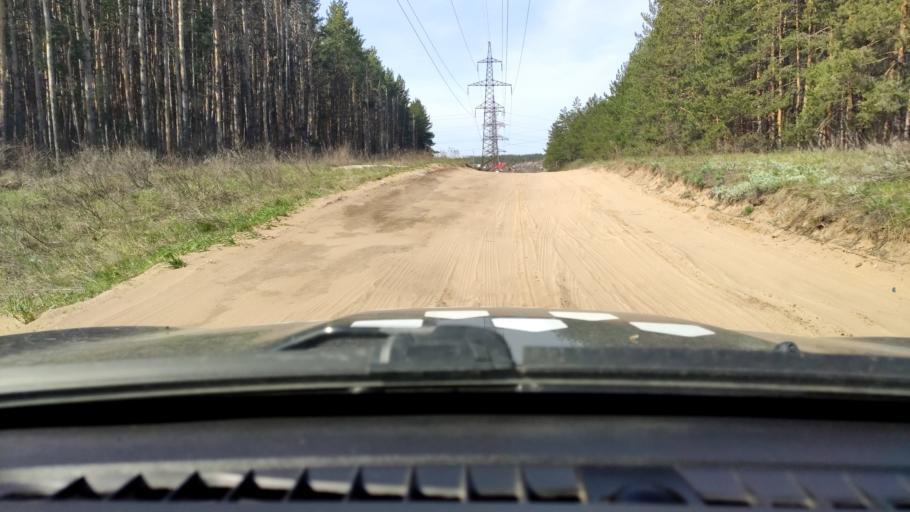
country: RU
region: Samara
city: Zhigulevsk
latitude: 53.4965
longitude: 49.5035
